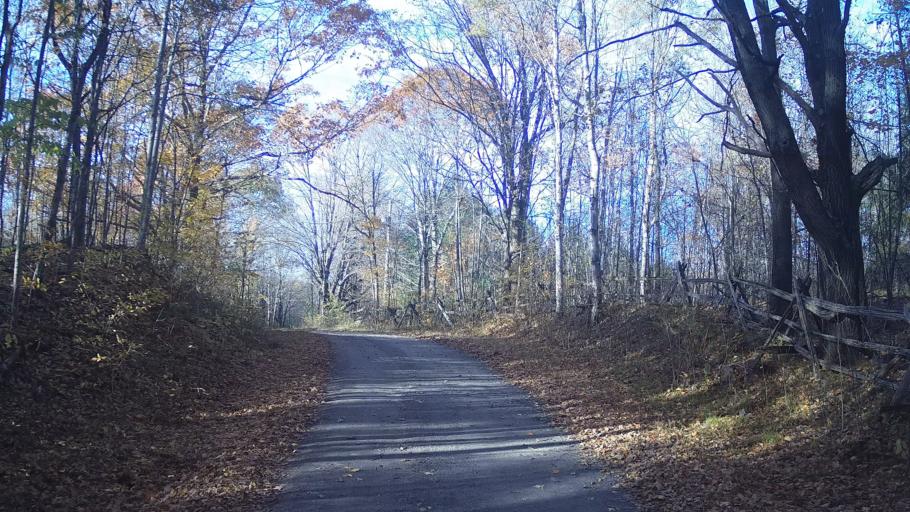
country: CA
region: Ontario
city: Perth
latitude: 44.7401
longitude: -76.4121
